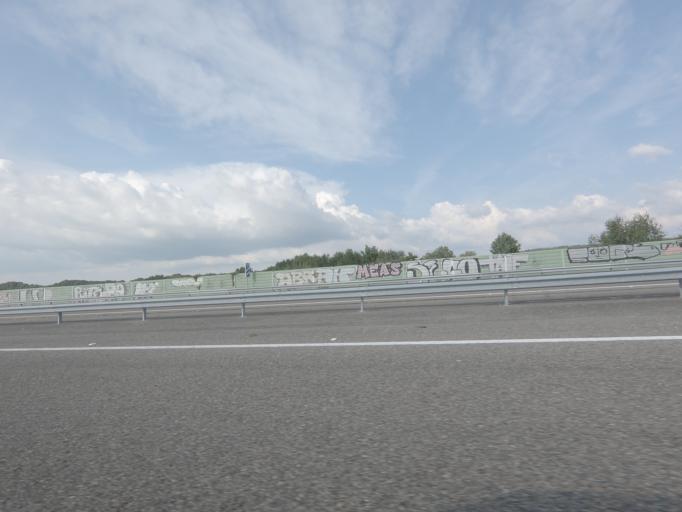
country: ES
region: Galicia
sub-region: Provincia de Ourense
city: Xinzo de Limia
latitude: 42.0740
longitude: -7.7079
